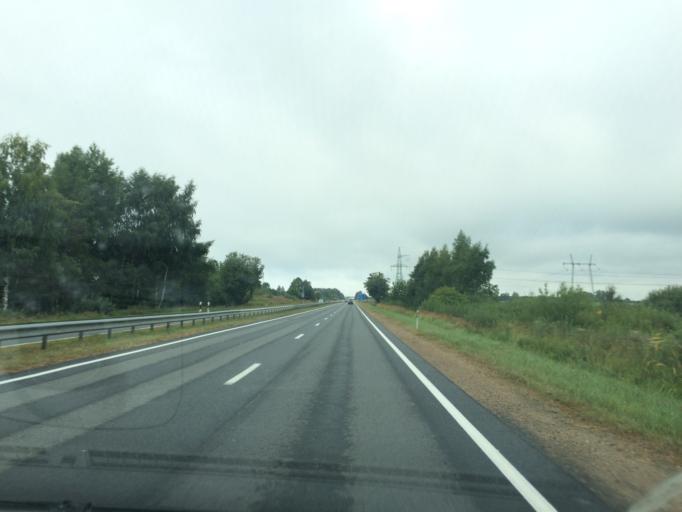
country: LV
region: Salaspils
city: Salaspils
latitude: 56.8467
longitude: 24.4162
